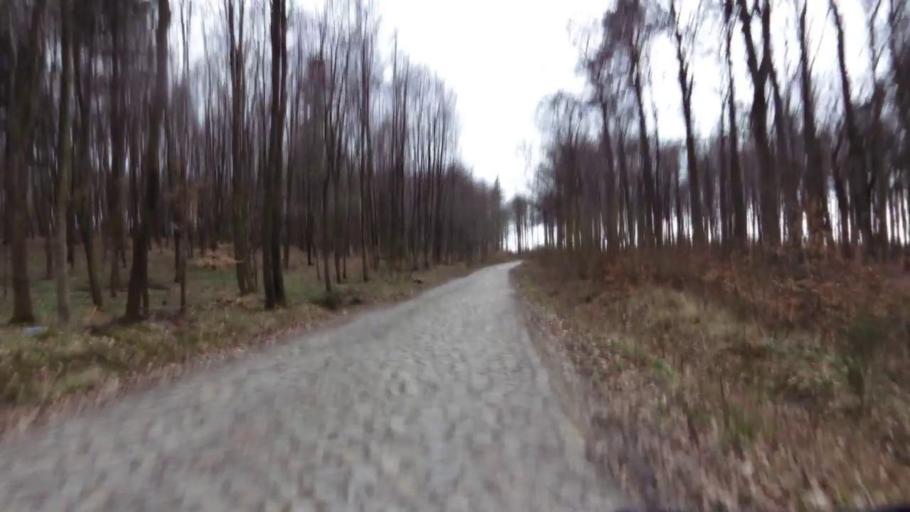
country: PL
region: West Pomeranian Voivodeship
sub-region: Powiat koszalinski
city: Sianow
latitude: 54.2708
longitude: 16.3200
